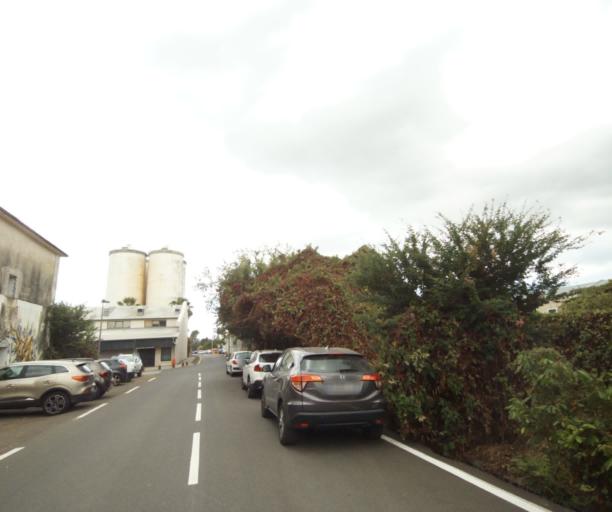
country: RE
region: Reunion
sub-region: Reunion
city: Saint-Paul
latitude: -20.9884
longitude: 55.2986
